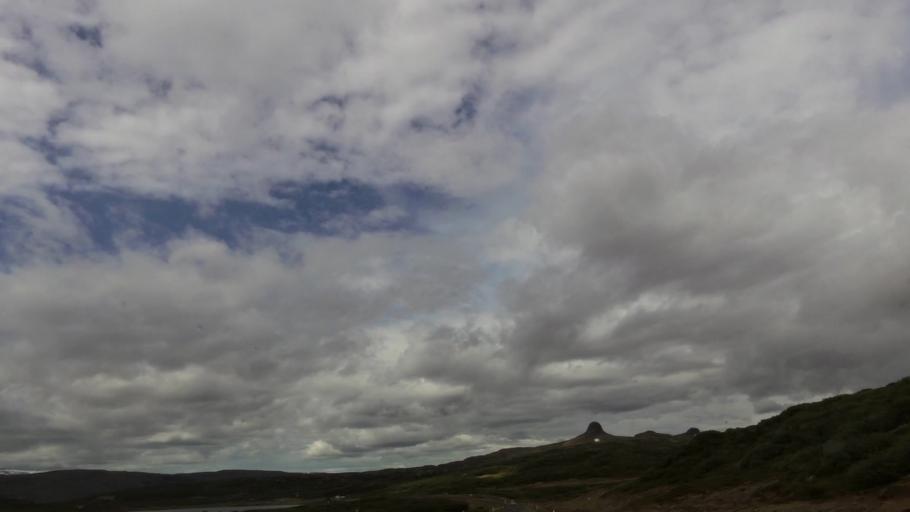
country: IS
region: West
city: Stykkisholmur
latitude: 65.5413
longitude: -22.0962
